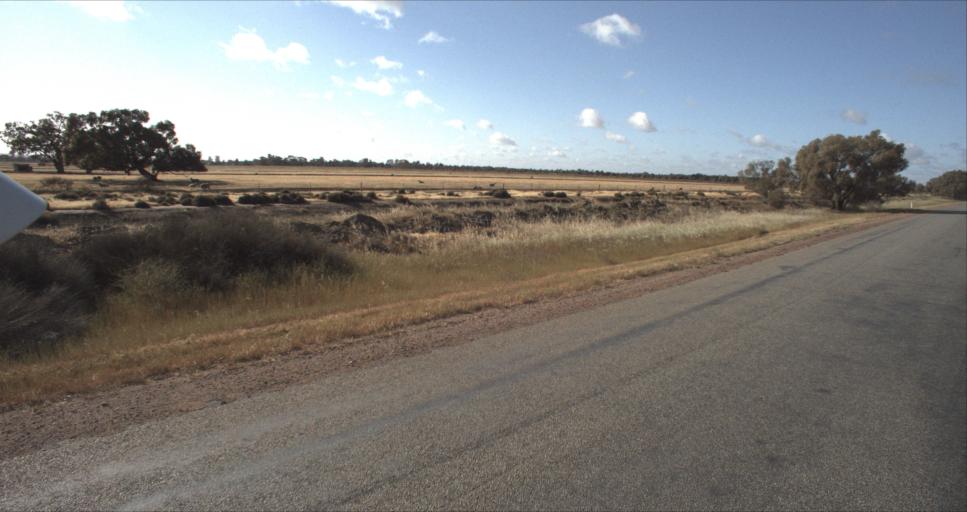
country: AU
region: New South Wales
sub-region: Leeton
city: Leeton
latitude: -34.5124
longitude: 146.3921
